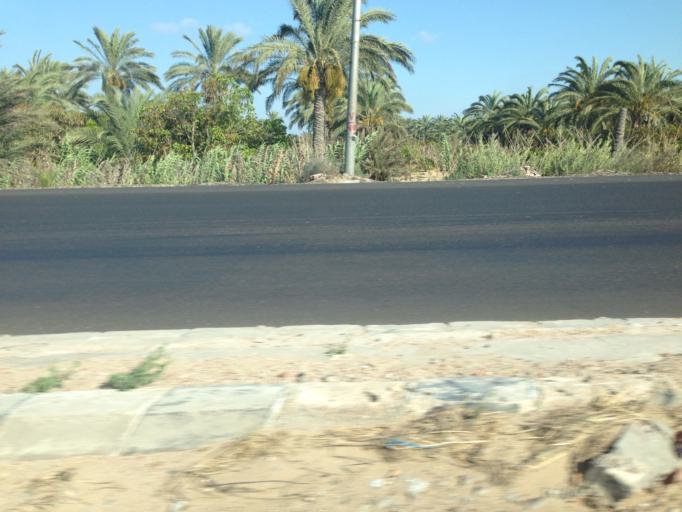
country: EG
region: Al Buhayrah
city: Idku
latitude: 31.3020
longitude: 30.2691
